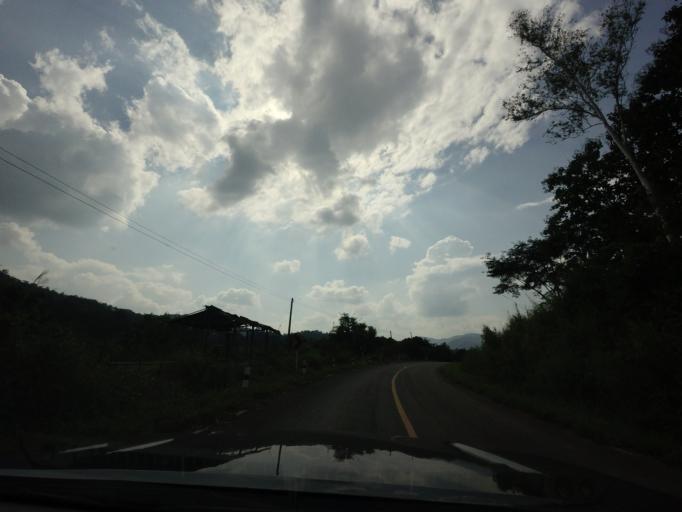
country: TH
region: Uttaradit
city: Ban Khok
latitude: 18.2290
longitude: 101.0213
